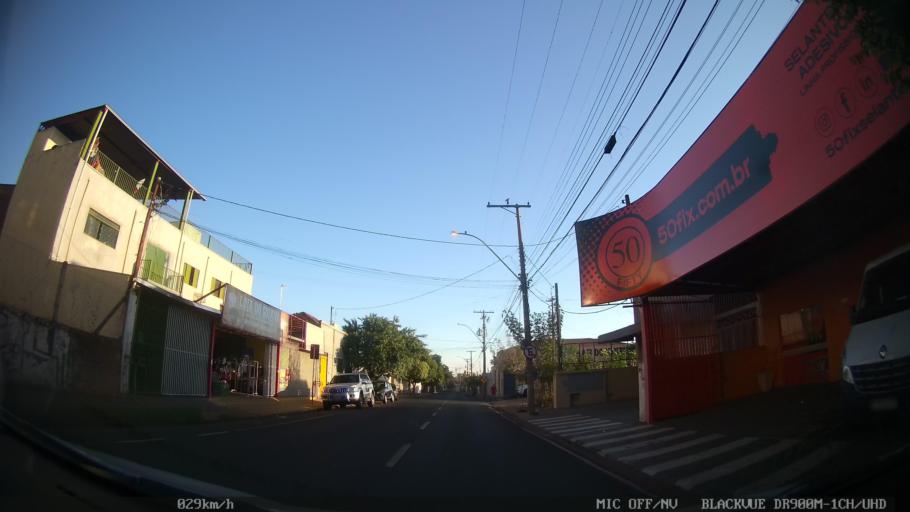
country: BR
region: Sao Paulo
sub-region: Sao Jose Do Rio Preto
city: Sao Jose do Rio Preto
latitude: -20.7998
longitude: -49.3712
